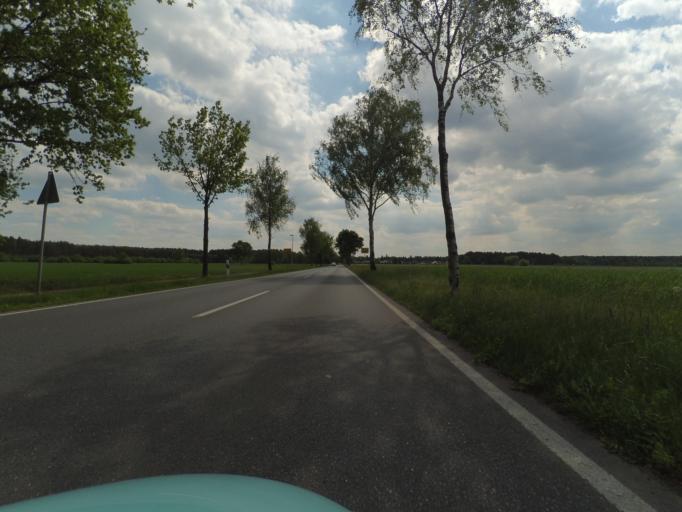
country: DE
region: Lower Saxony
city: Winsen
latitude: 52.6497
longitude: 9.9329
